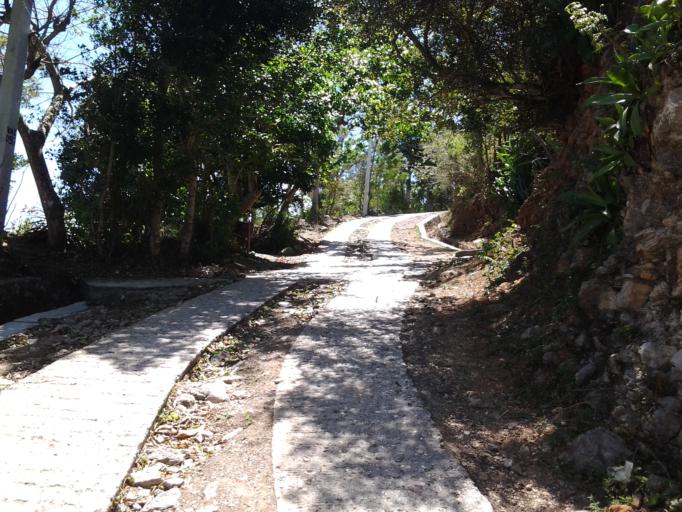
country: HT
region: Ouest
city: Grangwav
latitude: 18.3963
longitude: -72.8144
